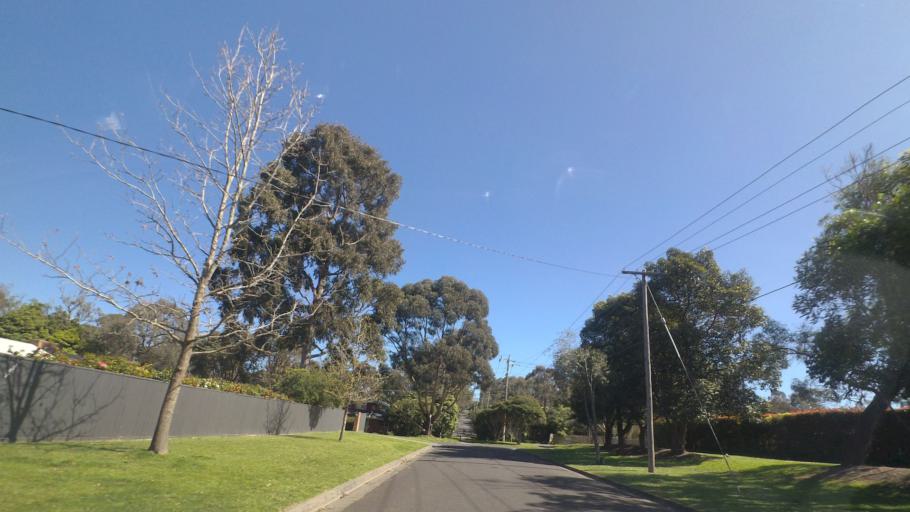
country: AU
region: Victoria
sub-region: Maroondah
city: Heathmont
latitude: -37.8351
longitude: 145.2509
